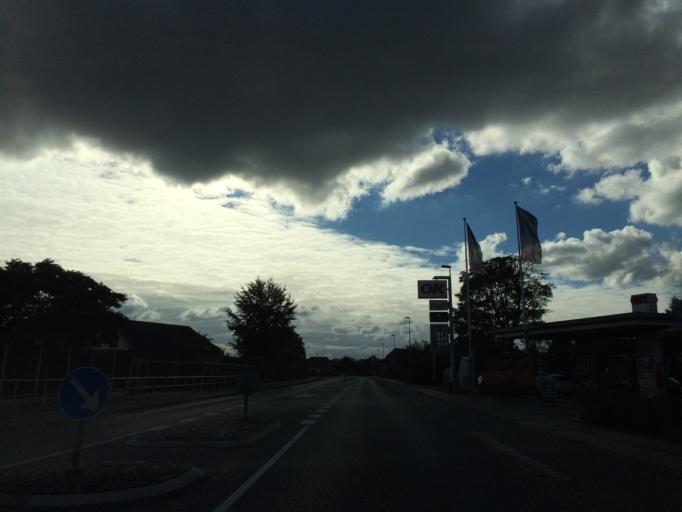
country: DK
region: Central Jutland
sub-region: Skanderborg Kommune
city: Ry
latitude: 56.0952
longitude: 9.7616
